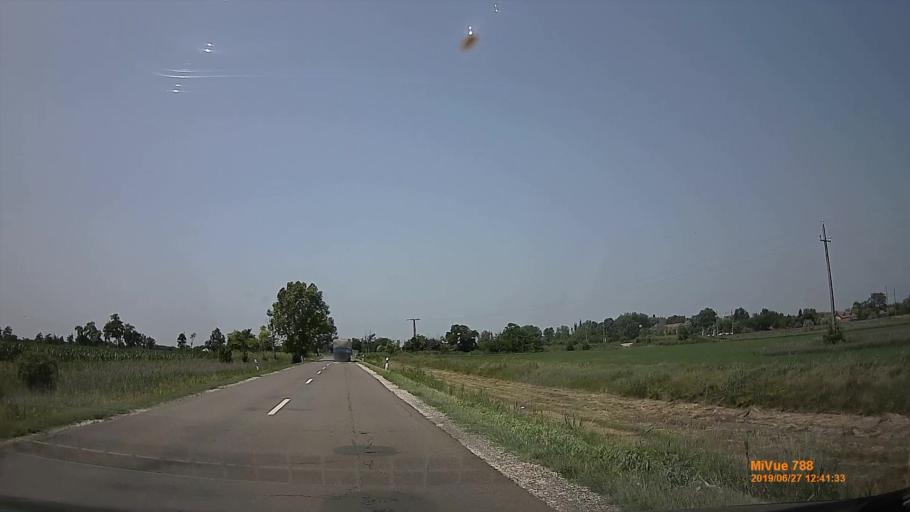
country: HU
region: Pest
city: Tortel
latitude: 47.1810
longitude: 19.8955
